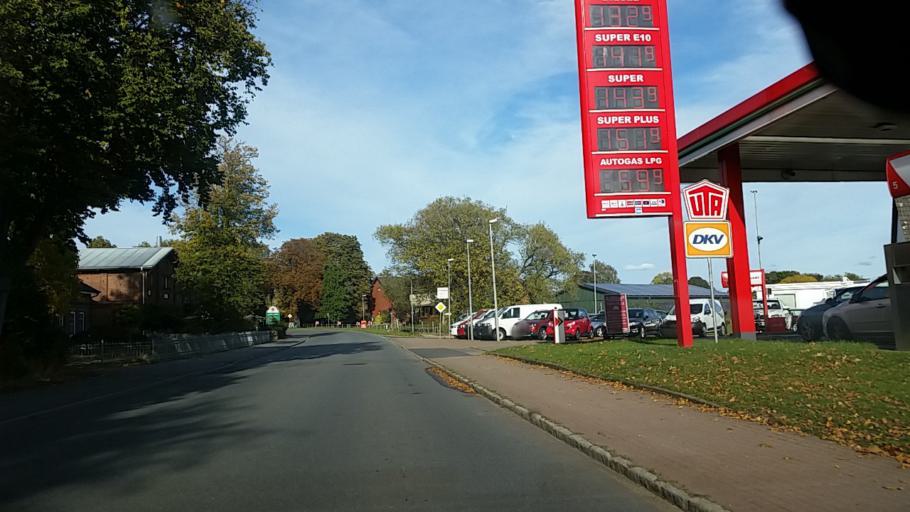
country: DE
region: Schleswig-Holstein
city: Delingsdorf
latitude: 53.7050
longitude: 10.2516
